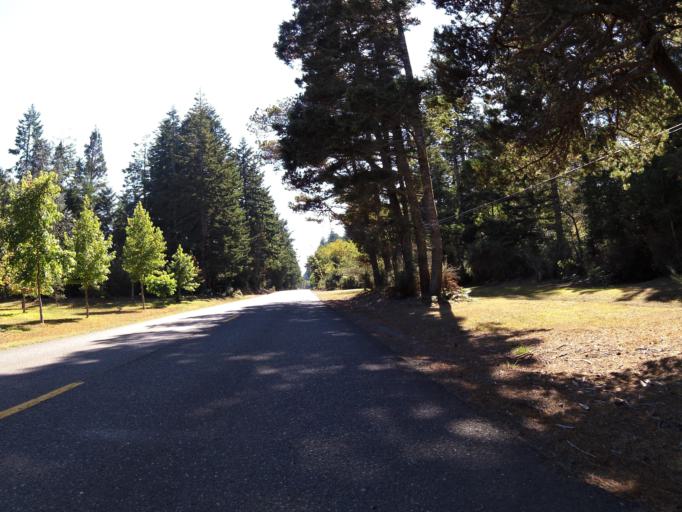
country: US
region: Oregon
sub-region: Coos County
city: Bandon
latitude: 43.1823
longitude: -124.3692
